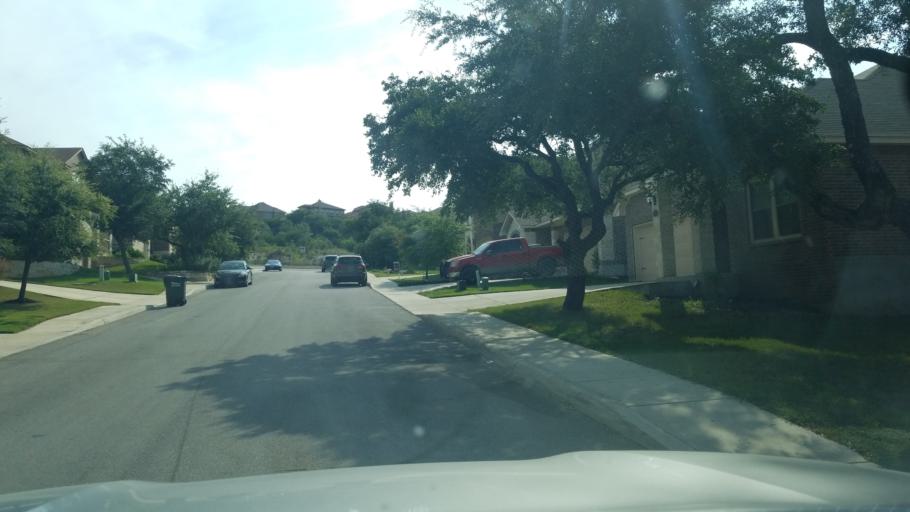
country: US
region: Texas
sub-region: Bexar County
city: Scenic Oaks
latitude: 29.7130
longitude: -98.6573
